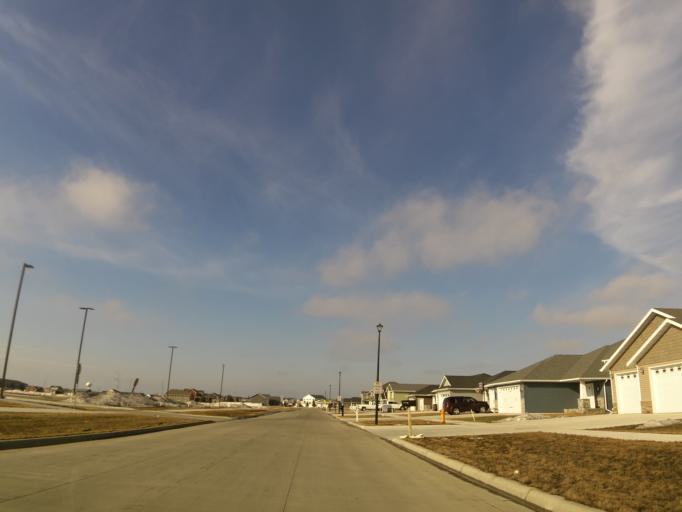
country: US
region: North Dakota
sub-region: Grand Forks County
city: Grand Forks
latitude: 47.8795
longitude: -97.0729
